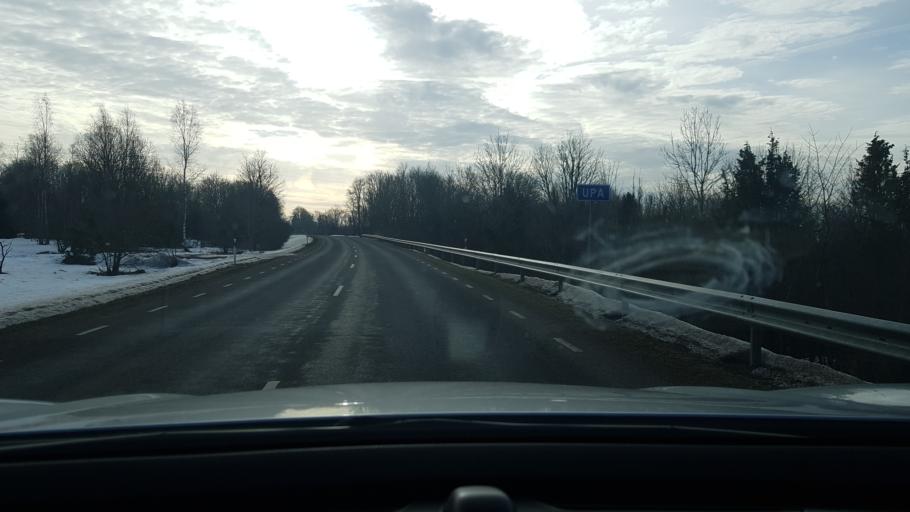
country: EE
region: Saare
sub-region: Kuressaare linn
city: Kuressaare
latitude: 58.3003
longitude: 22.5394
